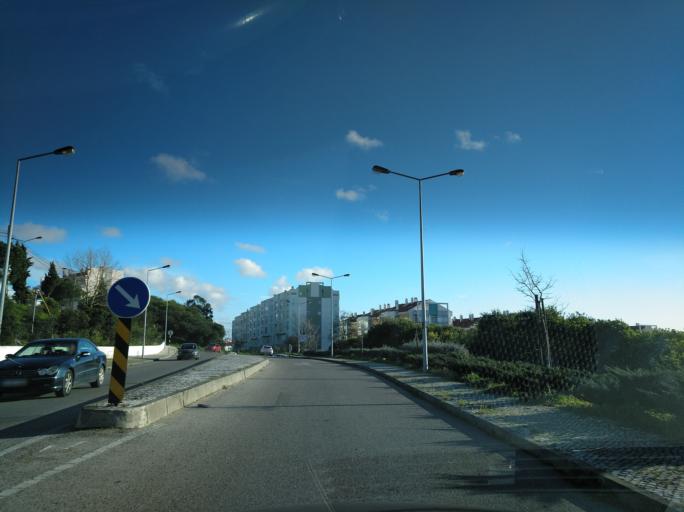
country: PT
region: Setubal
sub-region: Almada
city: Sobreda
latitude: 38.6532
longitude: -9.1875
